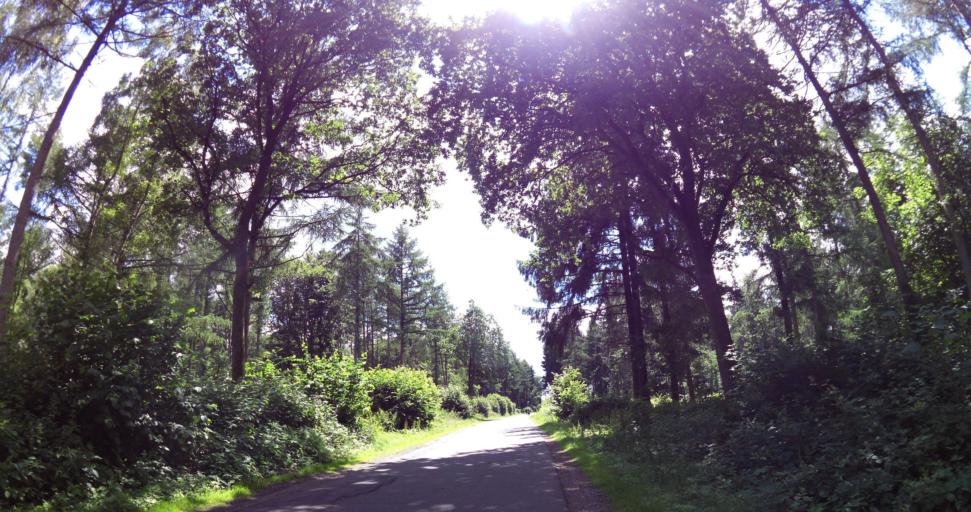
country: DE
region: Schleswig-Holstein
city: Brodersby
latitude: 54.5083
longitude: 9.7207
